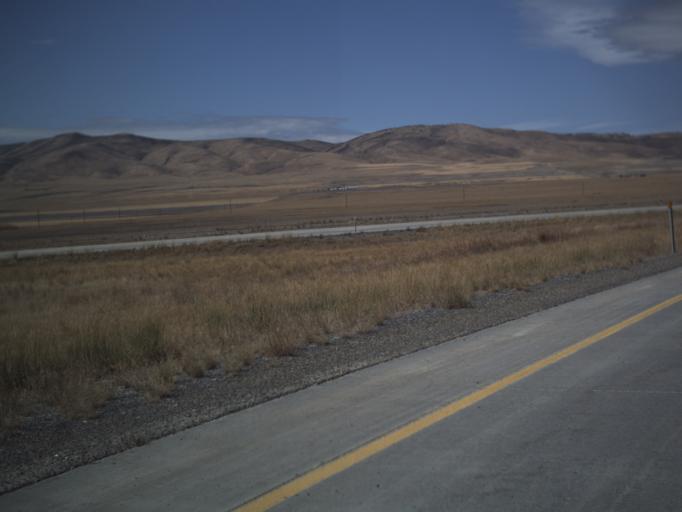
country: US
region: Utah
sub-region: Box Elder County
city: Garland
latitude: 41.8430
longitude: -112.4377
